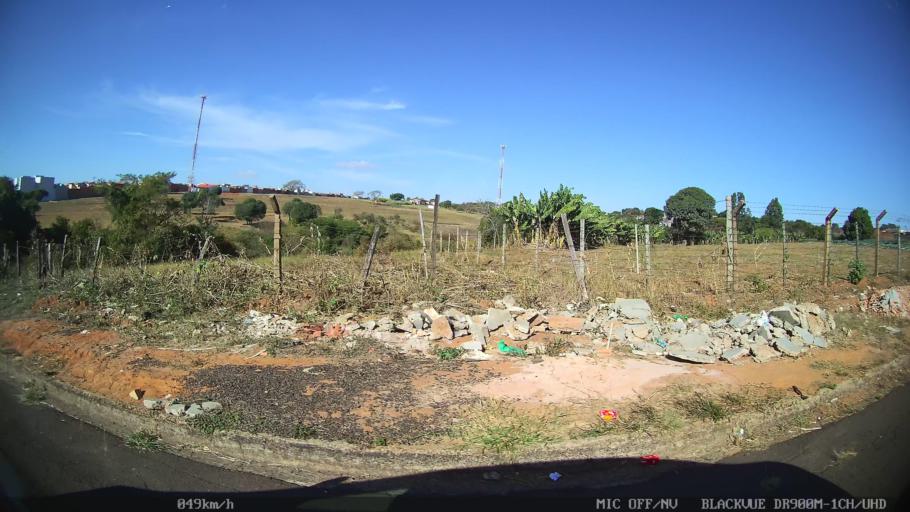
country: BR
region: Sao Paulo
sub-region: Franca
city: Franca
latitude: -20.4942
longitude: -47.4139
